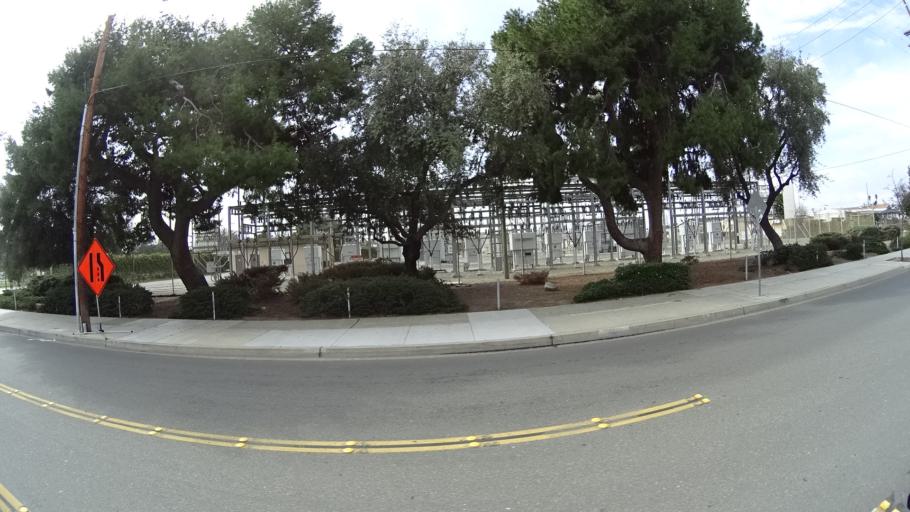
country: US
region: California
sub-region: Orange County
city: Buena Park
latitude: 33.8374
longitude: -117.9677
